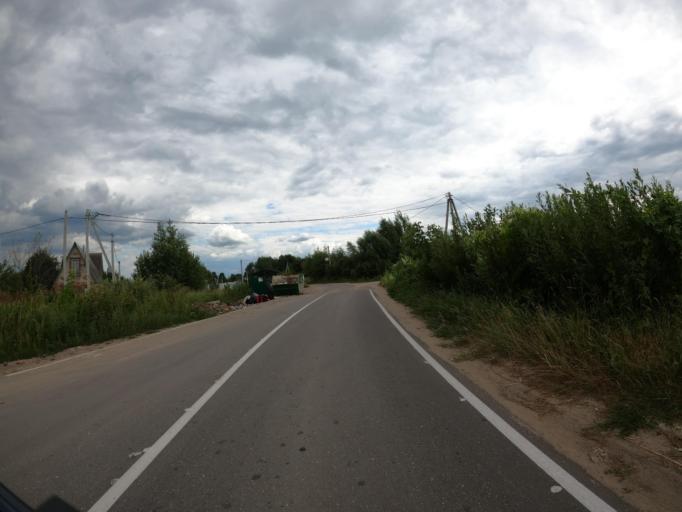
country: RU
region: Moskovskaya
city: Bronnitsy
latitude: 55.4868
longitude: 38.2524
